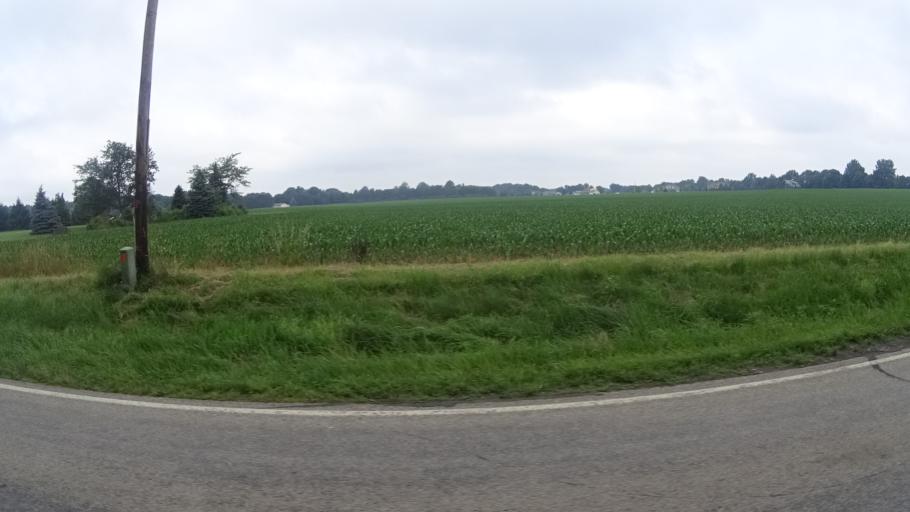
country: US
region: Ohio
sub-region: Huron County
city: Wakeman
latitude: 41.2977
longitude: -82.4926
